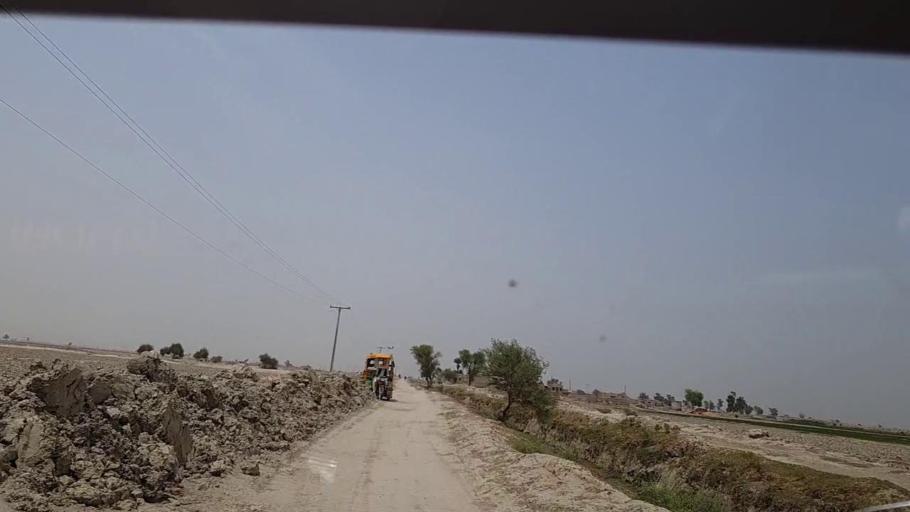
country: PK
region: Sindh
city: Khairpur Nathan Shah
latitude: 27.0508
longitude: 67.6192
